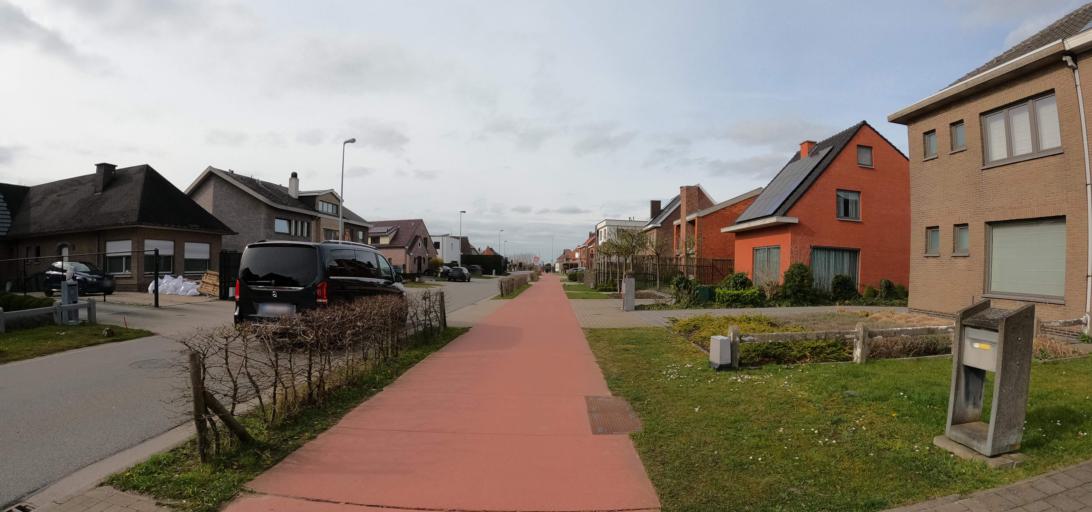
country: BE
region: Flanders
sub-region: Provincie Oost-Vlaanderen
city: Sint-Niklaas
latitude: 51.1850
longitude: 4.1642
